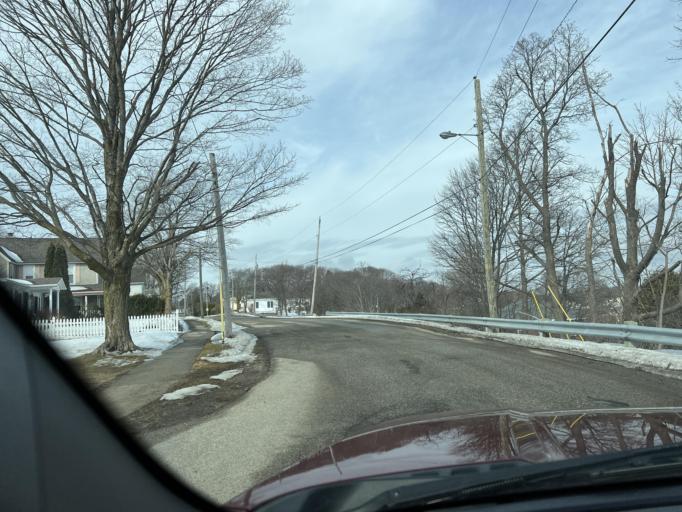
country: US
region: Michigan
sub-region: Mackinac County
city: Saint Ignace
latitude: 45.8674
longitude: -84.7267
